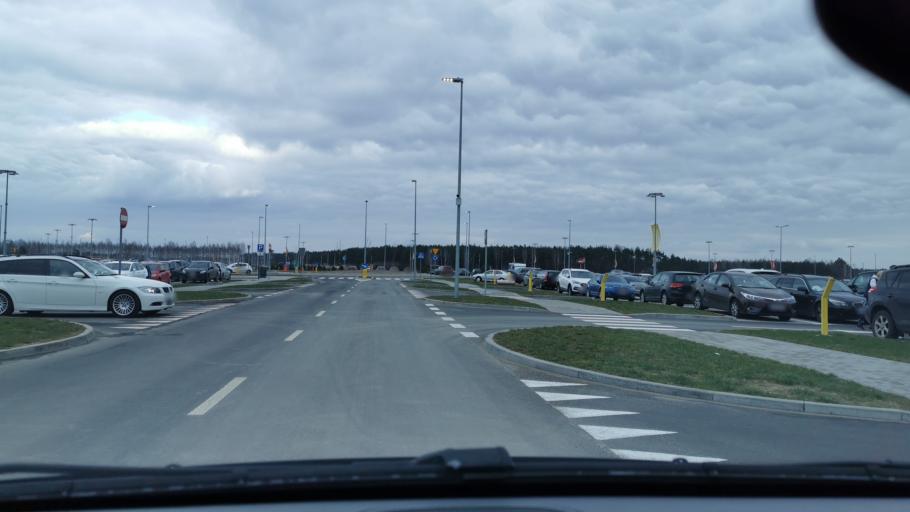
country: PL
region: Masovian Voivodeship
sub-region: Powiat zyrardowski
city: Mszczonow
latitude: 51.9868
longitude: 20.4609
